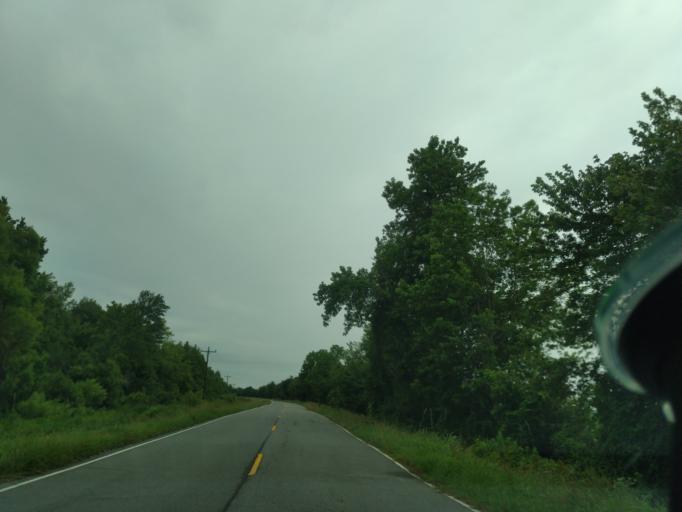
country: US
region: North Carolina
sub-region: Washington County
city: Plymouth
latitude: 35.7815
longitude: -76.5231
